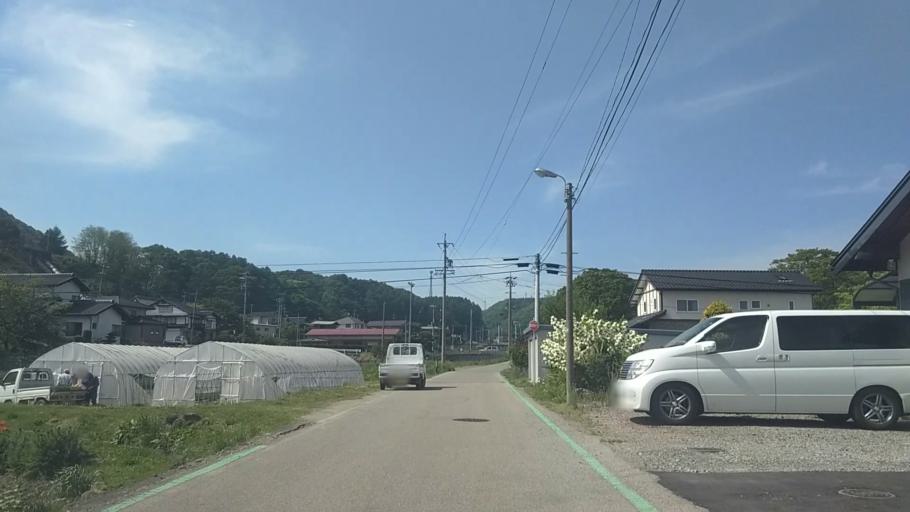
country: JP
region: Nagano
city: Saku
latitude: 36.1327
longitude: 138.4747
